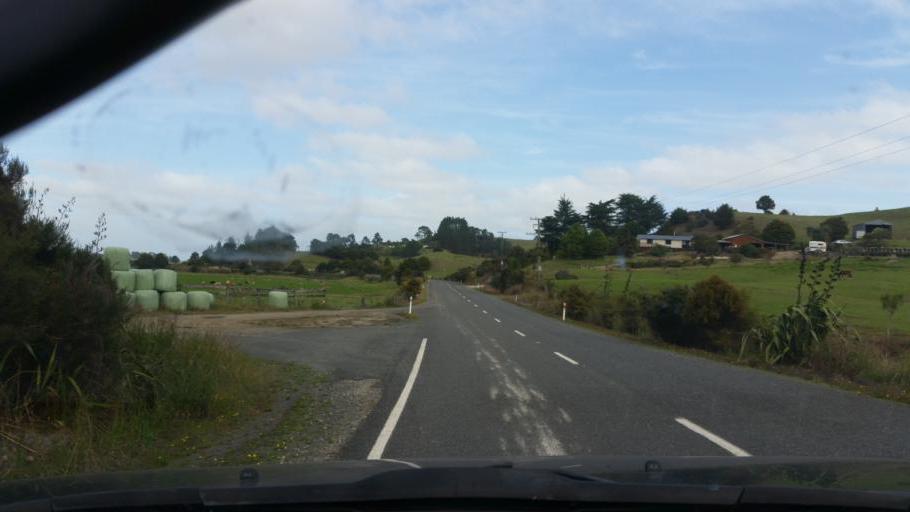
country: NZ
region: Northland
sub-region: Kaipara District
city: Dargaville
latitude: -35.8862
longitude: 173.8417
